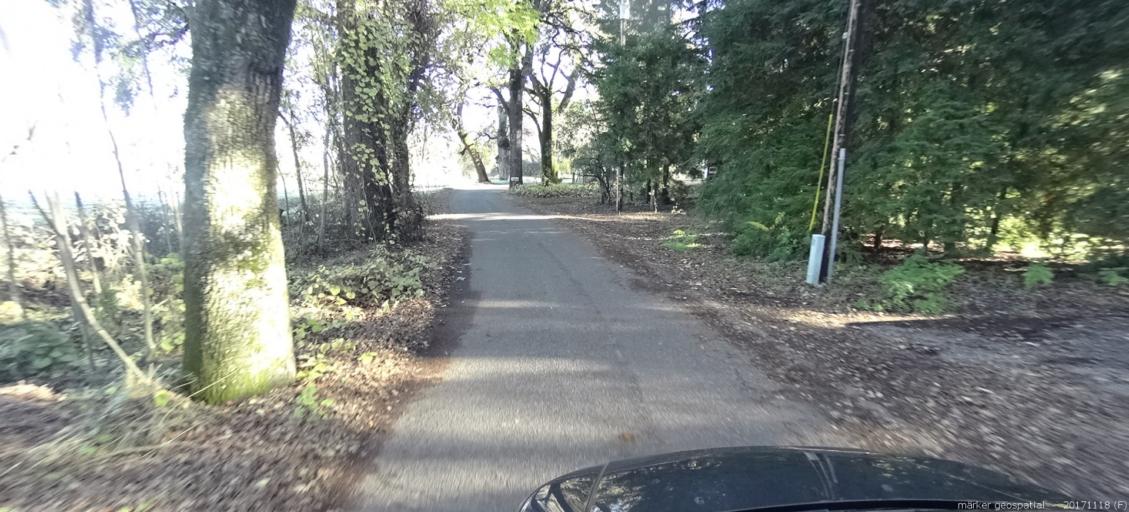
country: US
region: California
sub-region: Shasta County
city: Anderson
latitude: 40.4604
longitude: -122.2419
